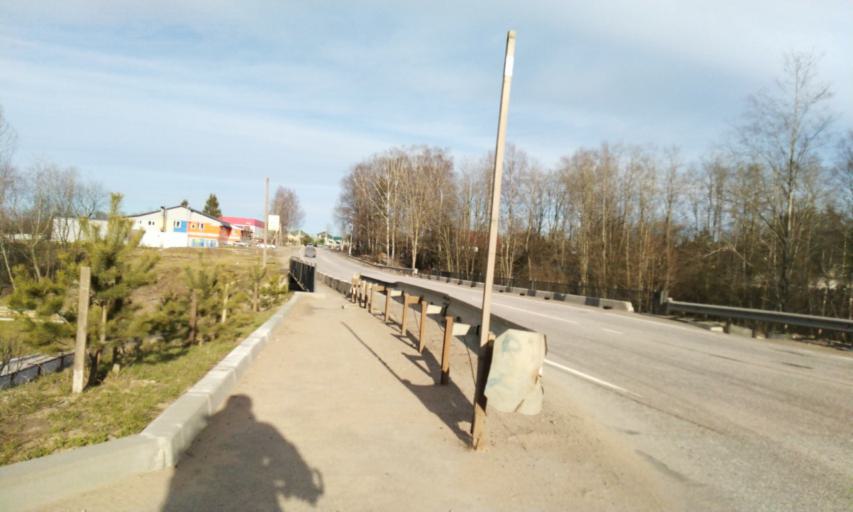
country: RU
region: Leningrad
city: Bugry
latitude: 60.1103
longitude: 30.4233
